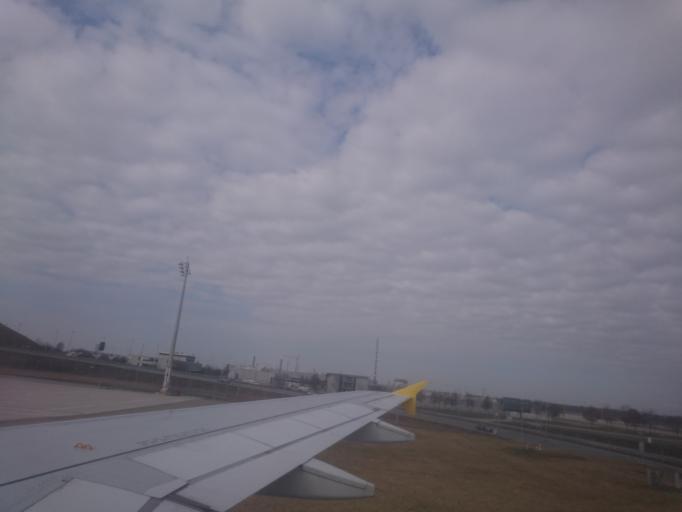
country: DE
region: Bavaria
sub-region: Upper Bavaria
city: Hallbergmoos
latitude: 48.3579
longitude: 11.7770
